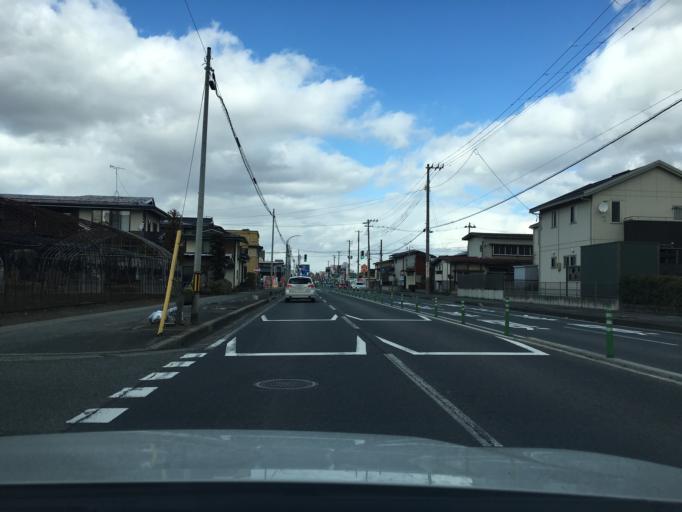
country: JP
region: Yamagata
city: Yamagata-shi
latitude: 38.2344
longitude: 140.3057
